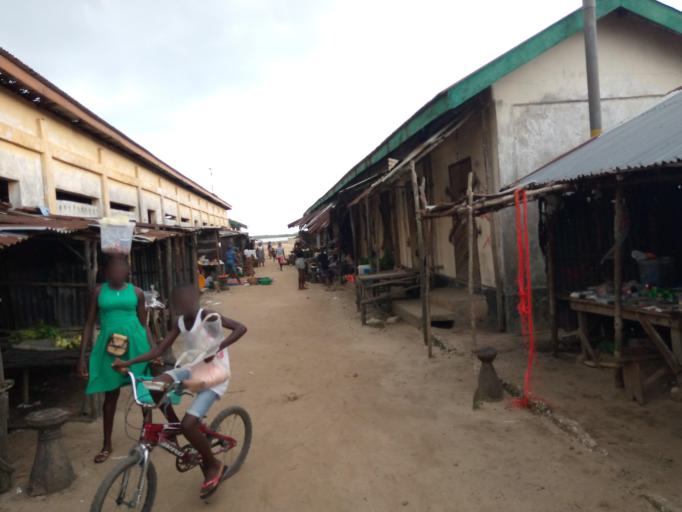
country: SL
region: Southern Province
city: Bonthe
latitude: 7.5291
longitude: -12.5014
